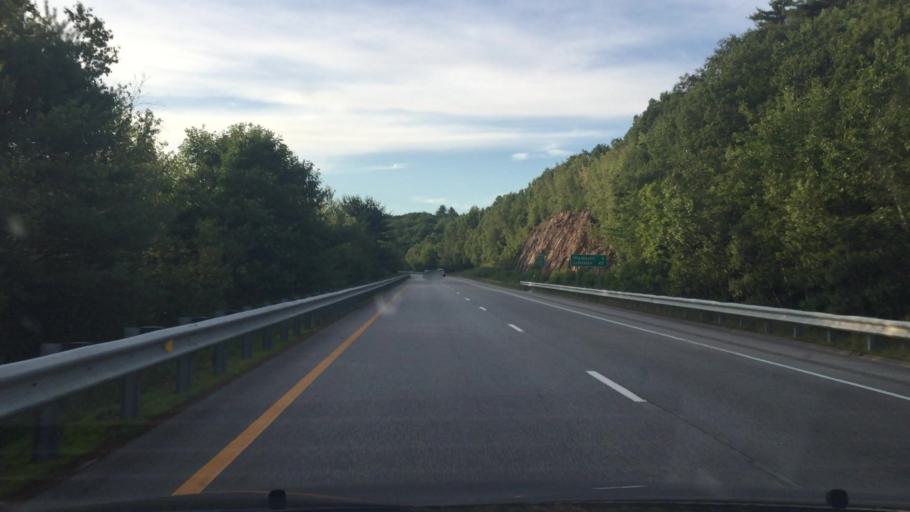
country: US
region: New Hampshire
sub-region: Grafton County
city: Ashland
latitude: 43.7097
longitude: -71.6503
